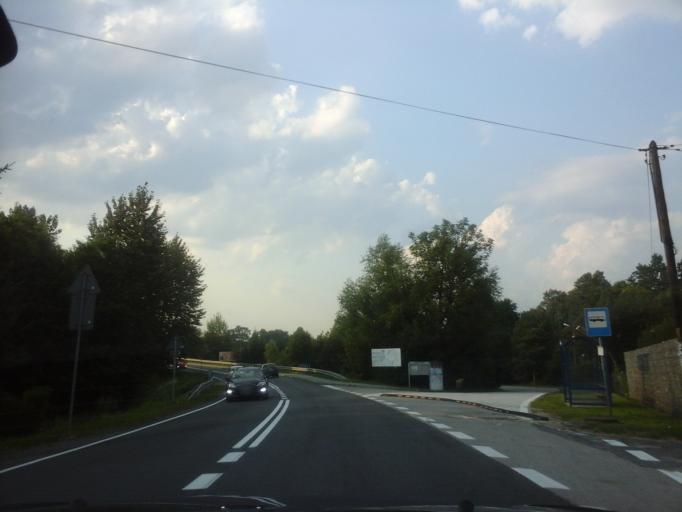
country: PL
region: Lesser Poland Voivodeship
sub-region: Powiat wadowicki
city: Ryczow
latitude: 49.9750
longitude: 19.5604
